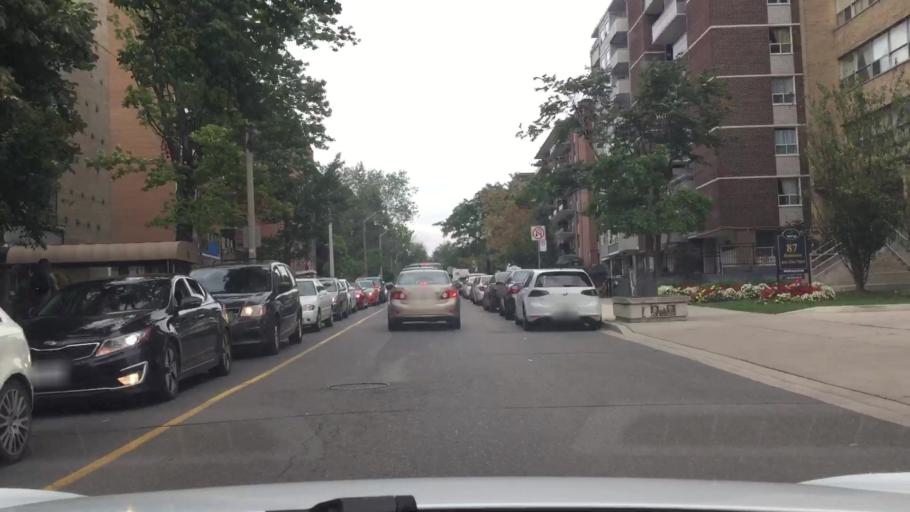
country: CA
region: Ontario
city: Toronto
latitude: 43.6345
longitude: -79.4349
